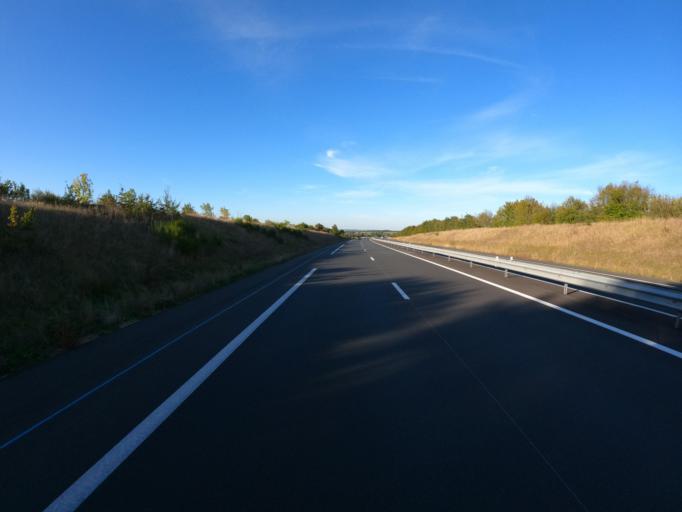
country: FR
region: Pays de la Loire
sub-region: Departement de la Vendee
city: Mortagne-sur-Sevre
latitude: 46.9849
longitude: -0.9176
